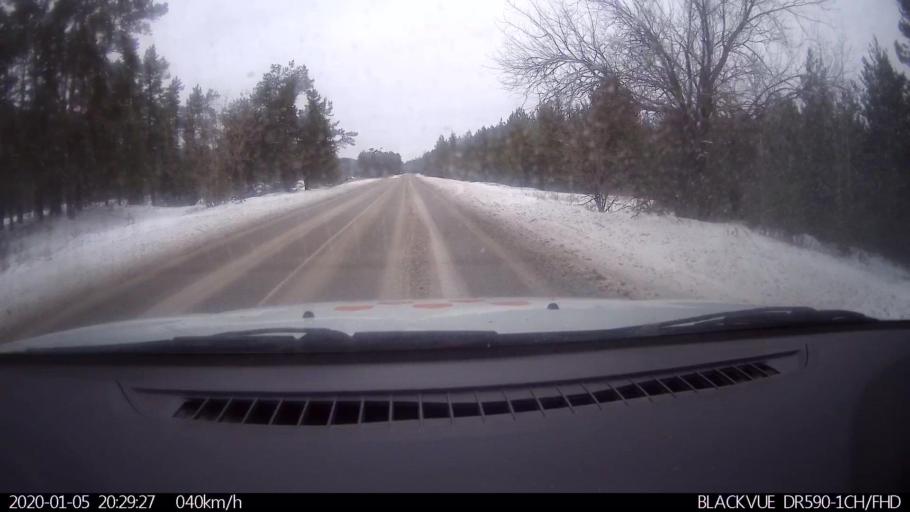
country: RU
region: Nizjnij Novgorod
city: Lukino
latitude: 56.3939
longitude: 43.7347
